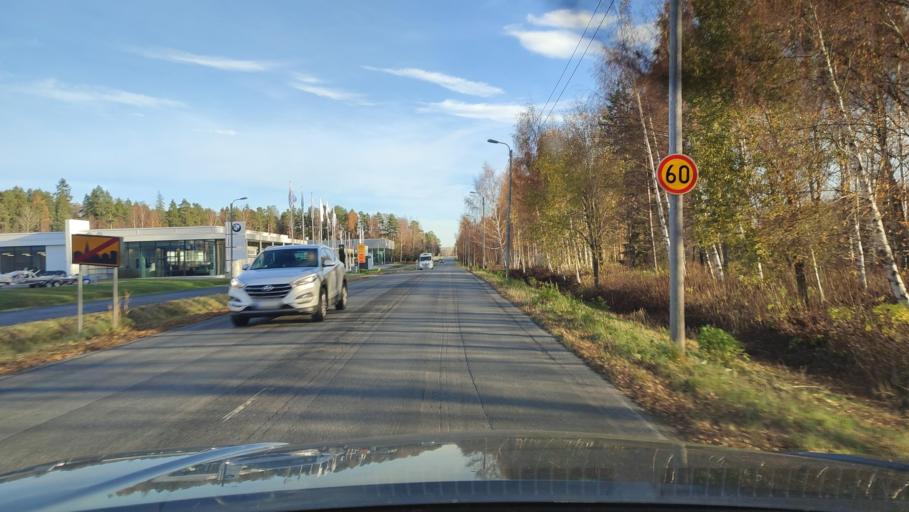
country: FI
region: Ostrobothnia
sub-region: Vaasa
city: Teeriniemi
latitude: 63.0793
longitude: 21.6615
